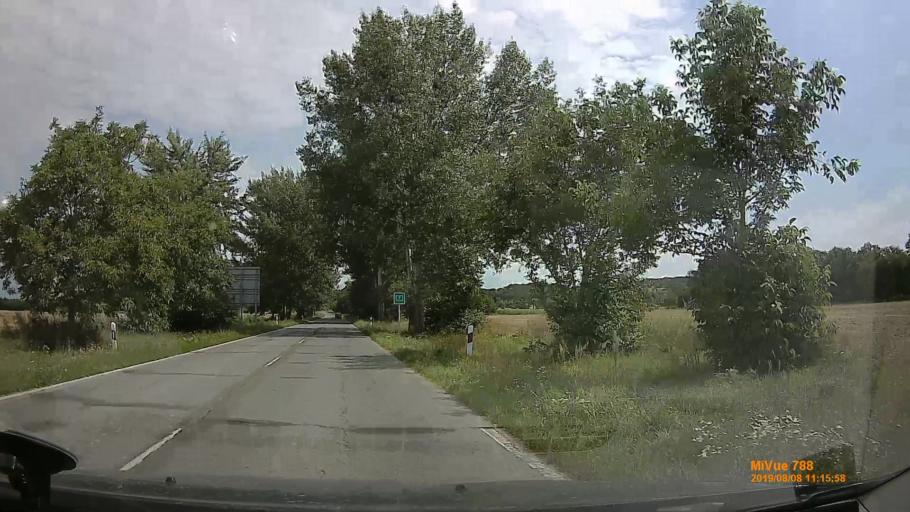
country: HU
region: Somogy
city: Balatonbereny
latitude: 46.6439
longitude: 17.3035
